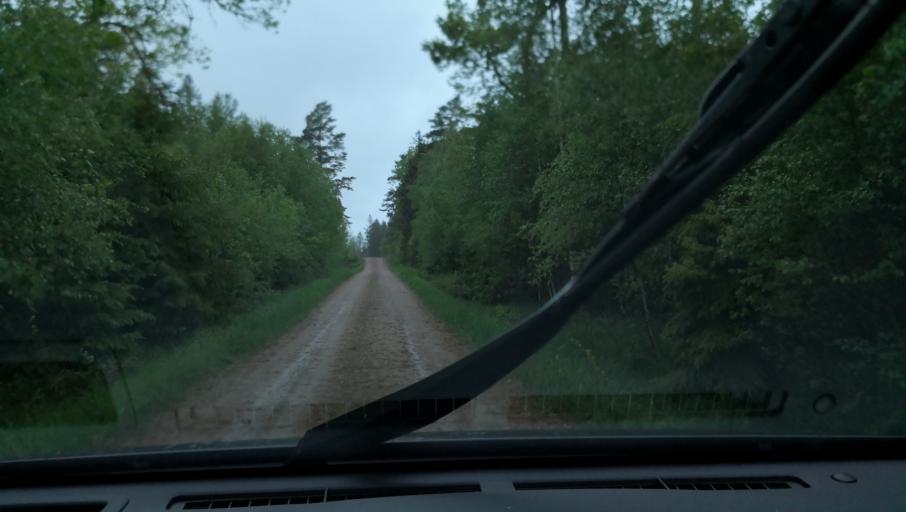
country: SE
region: Uppsala
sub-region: Enkopings Kommun
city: Orsundsbro
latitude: 59.9281
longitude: 17.3316
